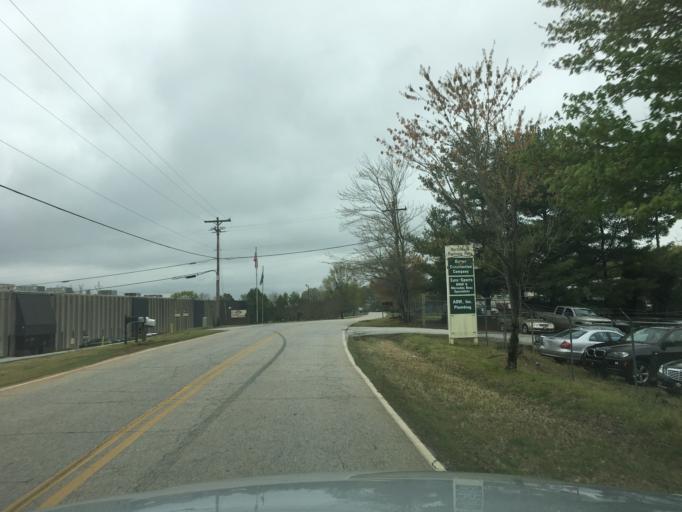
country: US
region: South Carolina
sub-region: Spartanburg County
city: Southern Shops
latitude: 34.9759
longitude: -82.0023
